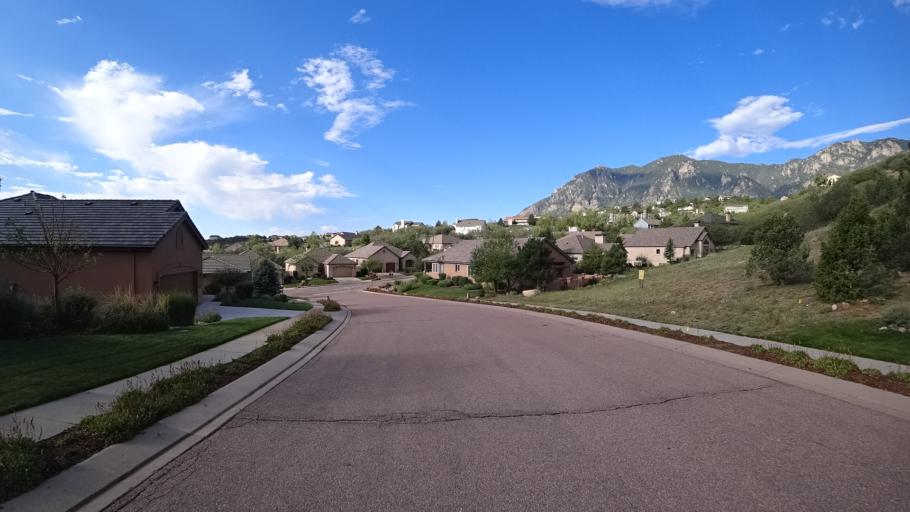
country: US
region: Colorado
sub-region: El Paso County
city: Stratmoor
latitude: 38.7655
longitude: -104.8204
